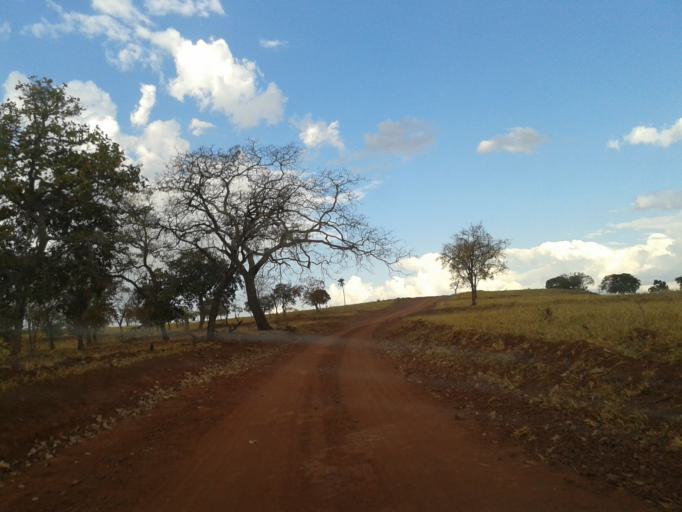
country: BR
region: Minas Gerais
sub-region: Santa Vitoria
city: Santa Vitoria
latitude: -19.1824
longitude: -49.9440
